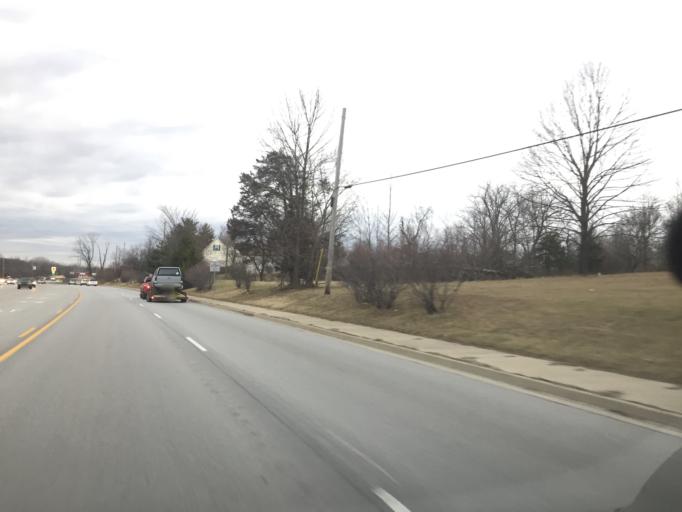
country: US
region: Indiana
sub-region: Monroe County
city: Ellettsville
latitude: 39.2112
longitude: -86.5848
